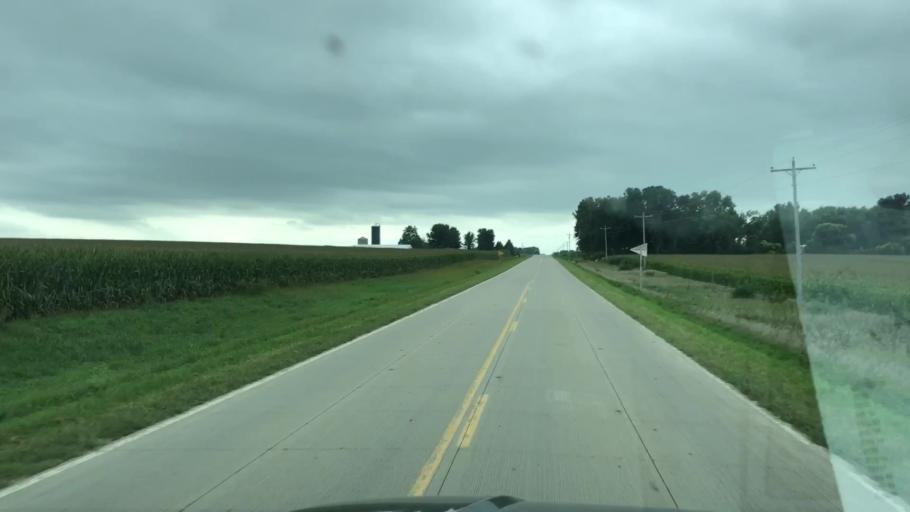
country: US
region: Iowa
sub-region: Sioux County
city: Alton
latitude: 43.0965
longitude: -95.9784
